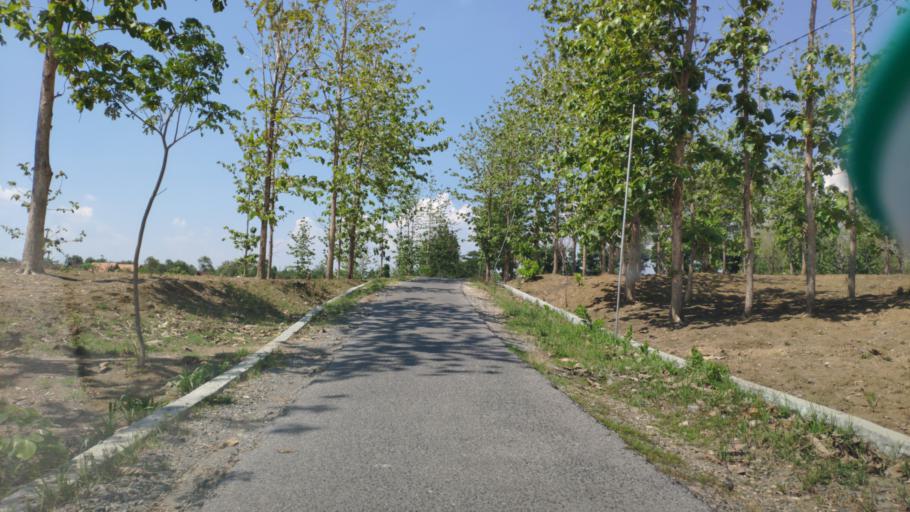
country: ID
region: Central Java
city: Galuk
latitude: -7.0885
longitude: 111.5030
